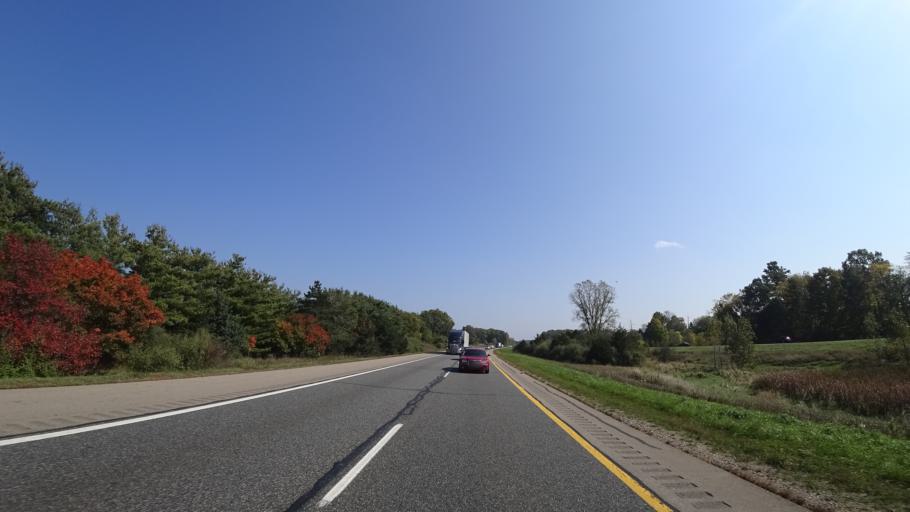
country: US
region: Michigan
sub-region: Washtenaw County
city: Dexter
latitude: 42.2998
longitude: -83.9495
